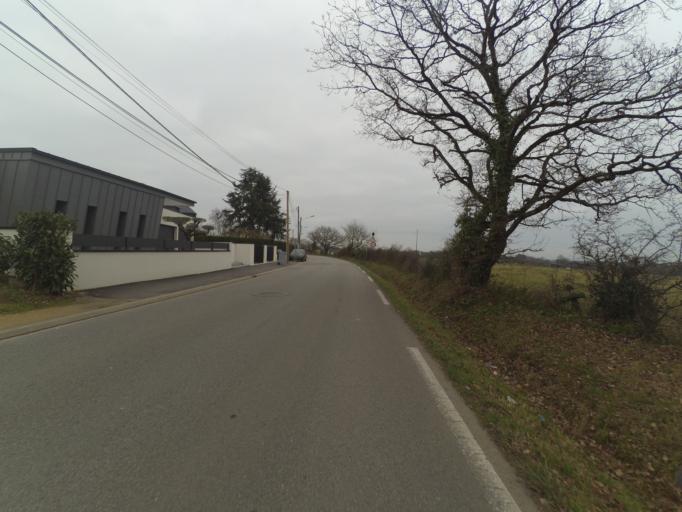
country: FR
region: Pays de la Loire
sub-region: Departement de la Loire-Atlantique
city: Saint-Herblain
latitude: 47.2217
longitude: -1.6658
